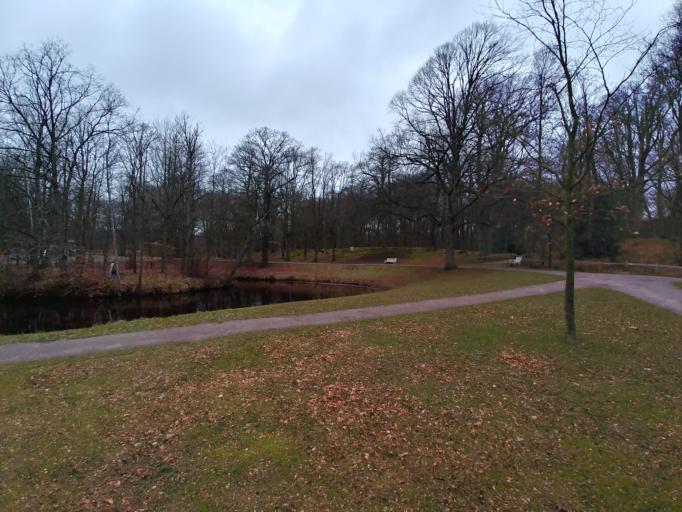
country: NL
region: South Holland
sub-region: Gemeente Leidschendam-Voorburg
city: Voorburg
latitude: 52.1017
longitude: 4.3327
